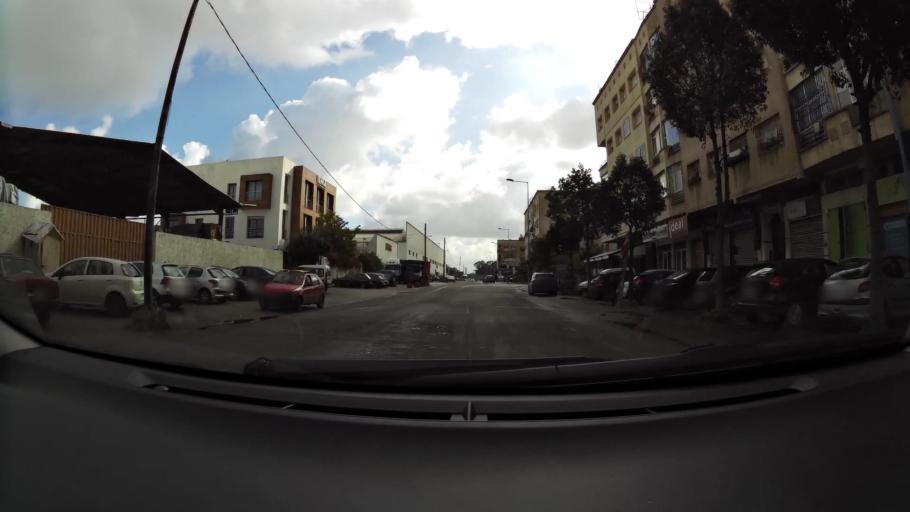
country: MA
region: Grand Casablanca
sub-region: Mediouna
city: Tit Mellil
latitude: 33.6025
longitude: -7.5375
